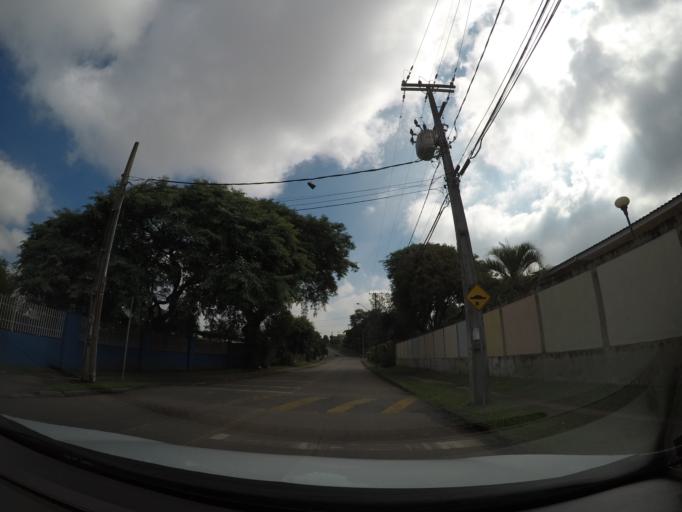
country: BR
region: Parana
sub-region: Sao Jose Dos Pinhais
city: Sao Jose dos Pinhais
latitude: -25.4921
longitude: -49.2236
